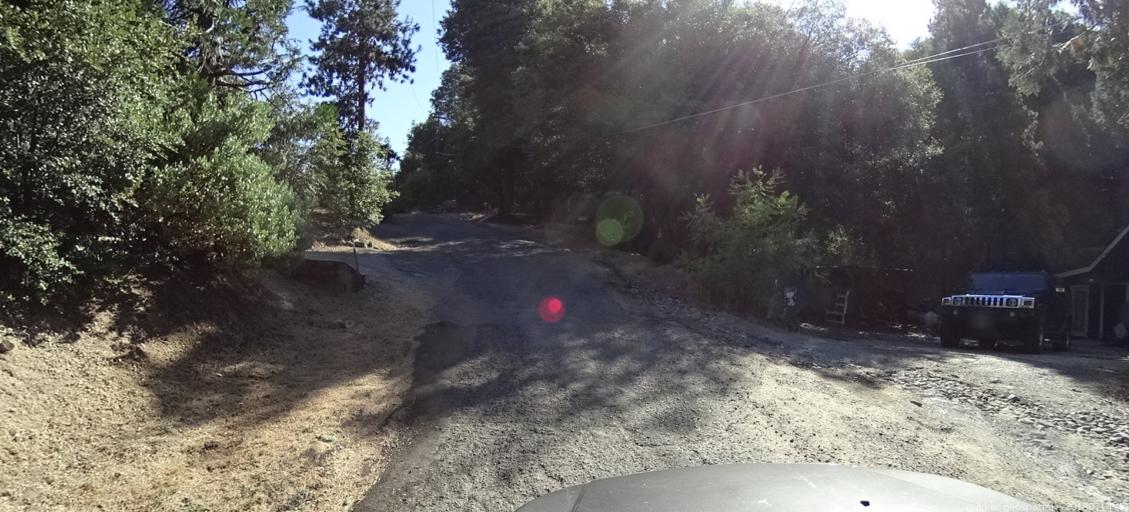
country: US
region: California
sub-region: Madera County
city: Oakhurst
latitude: 37.4003
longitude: -119.6179
